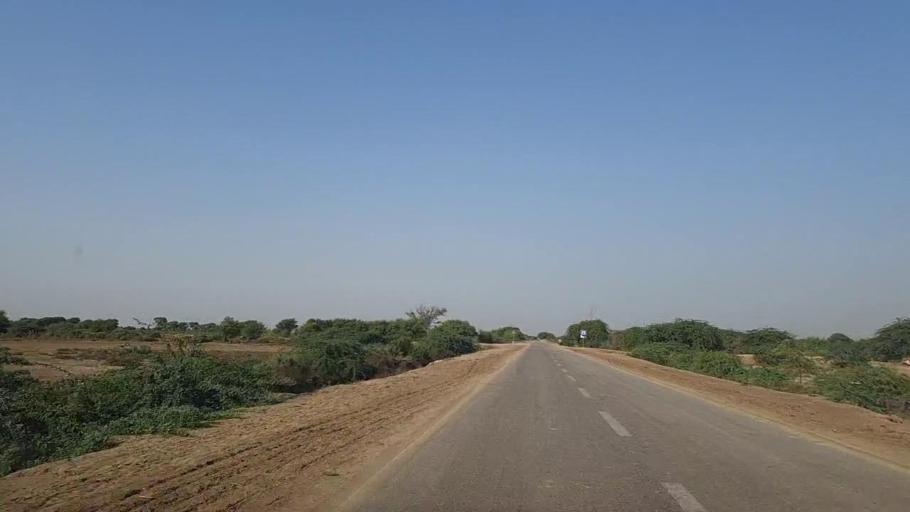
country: PK
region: Sindh
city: Mirpur Batoro
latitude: 24.5726
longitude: 68.3939
